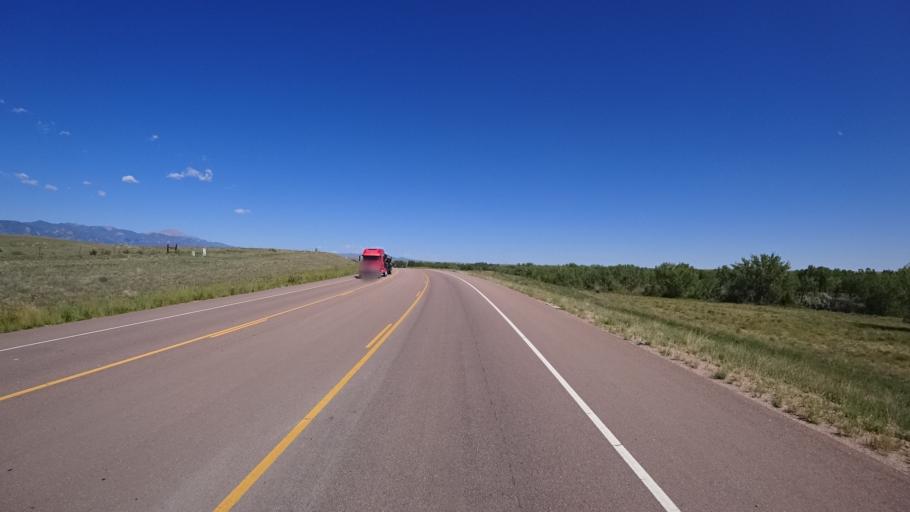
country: US
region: Colorado
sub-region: El Paso County
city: Security-Widefield
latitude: 38.7472
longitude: -104.6487
